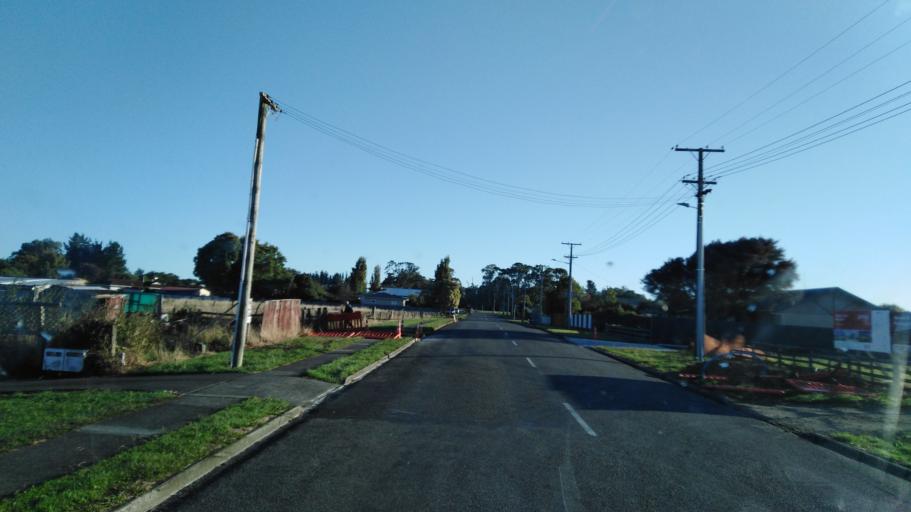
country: NZ
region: Manawatu-Wanganui
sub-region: Rangitikei District
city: Bulls
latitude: -40.0662
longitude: 175.3839
